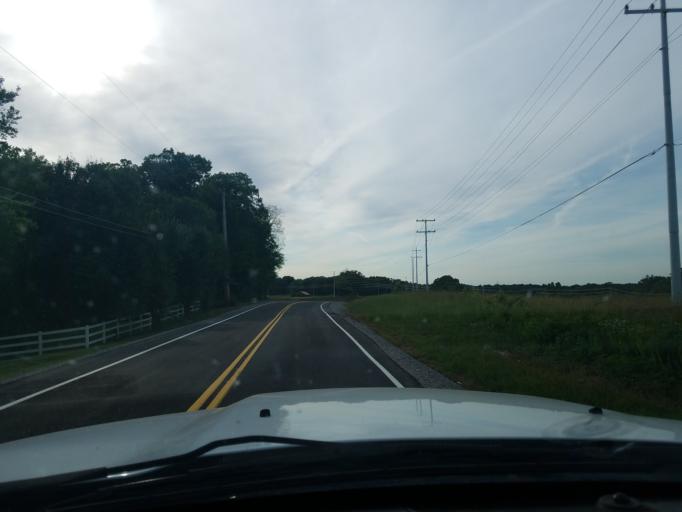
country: US
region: Tennessee
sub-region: Putnam County
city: Baxter
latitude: 36.1336
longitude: -85.5787
